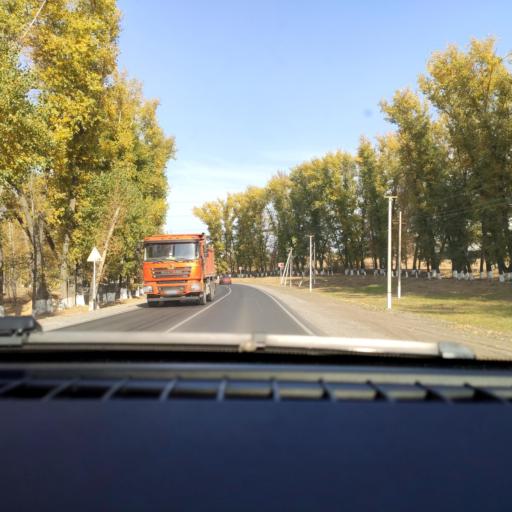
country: RU
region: Voronezj
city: Novaya Usman'
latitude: 51.6736
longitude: 39.4069
